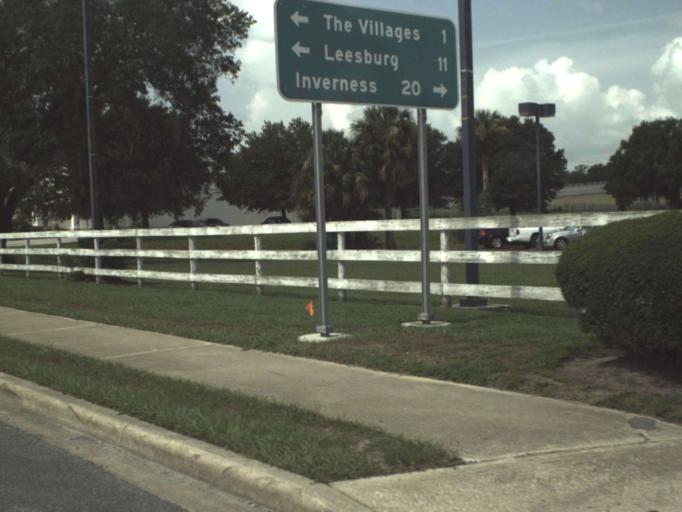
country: US
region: Florida
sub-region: Sumter County
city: Wildwood
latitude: 28.8487
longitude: -82.0455
